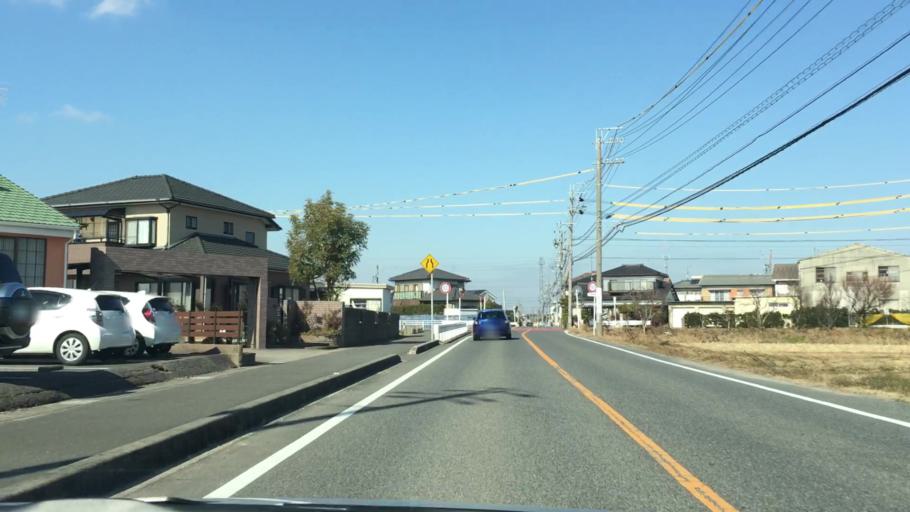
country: JP
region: Aichi
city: Anjo
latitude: 34.9872
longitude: 137.1171
